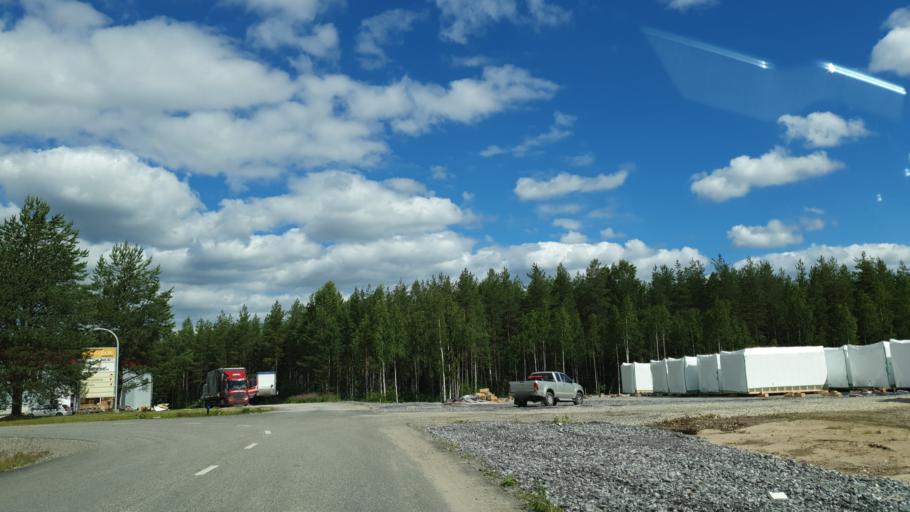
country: FI
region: Kainuu
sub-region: Kehys-Kainuu
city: Kuhmo
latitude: 64.1341
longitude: 29.4730
